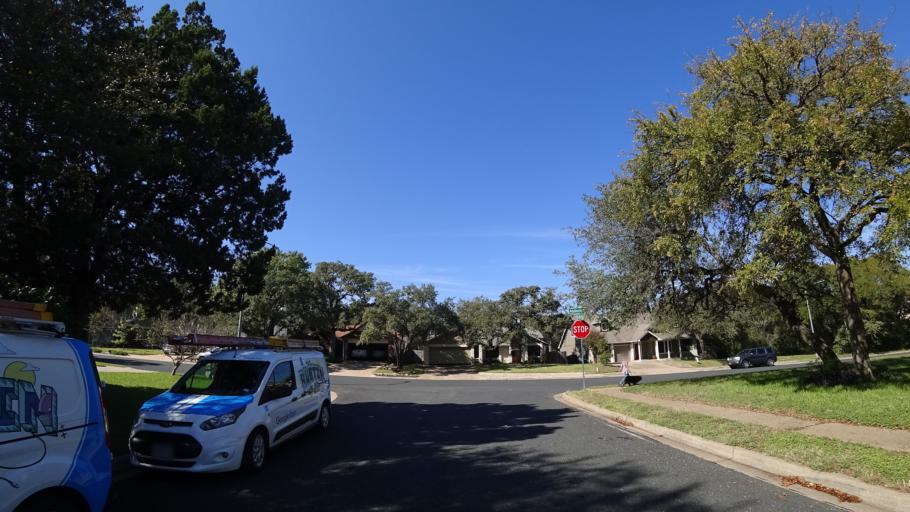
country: US
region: Texas
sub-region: Travis County
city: Shady Hollow
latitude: 30.2199
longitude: -97.8683
